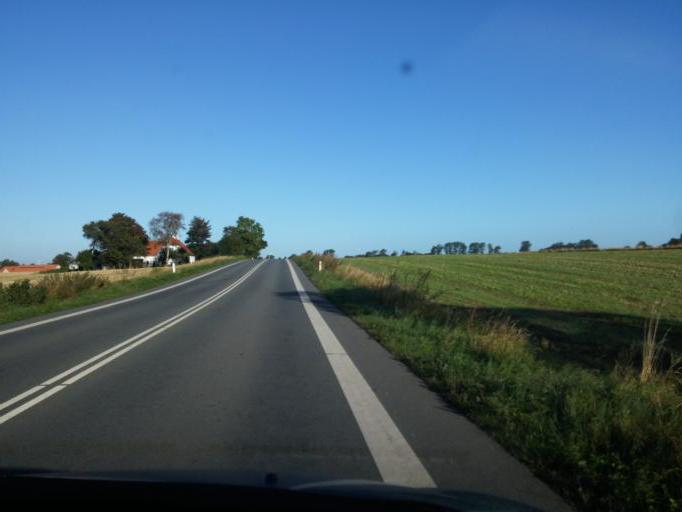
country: DK
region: South Denmark
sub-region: Kerteminde Kommune
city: Kerteminde
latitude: 55.4693
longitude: 10.6744
